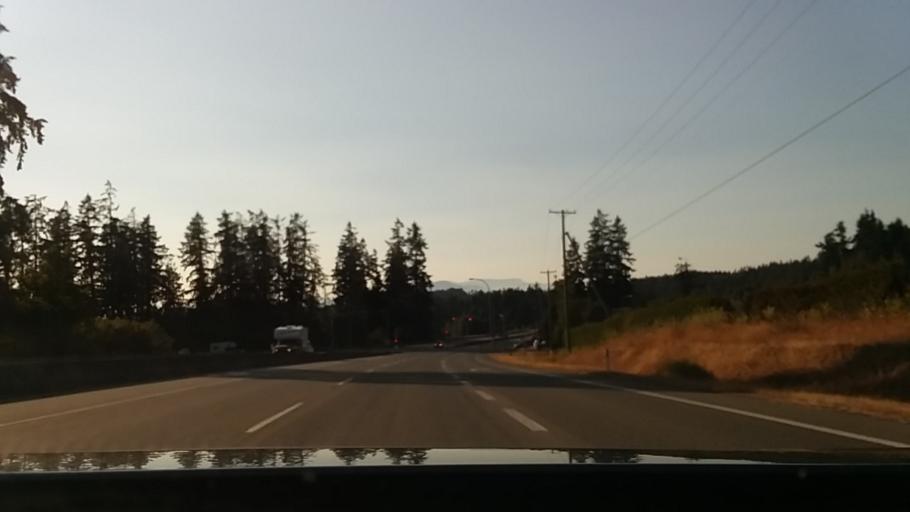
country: CA
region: British Columbia
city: Duncan
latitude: 48.7066
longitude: -123.6059
